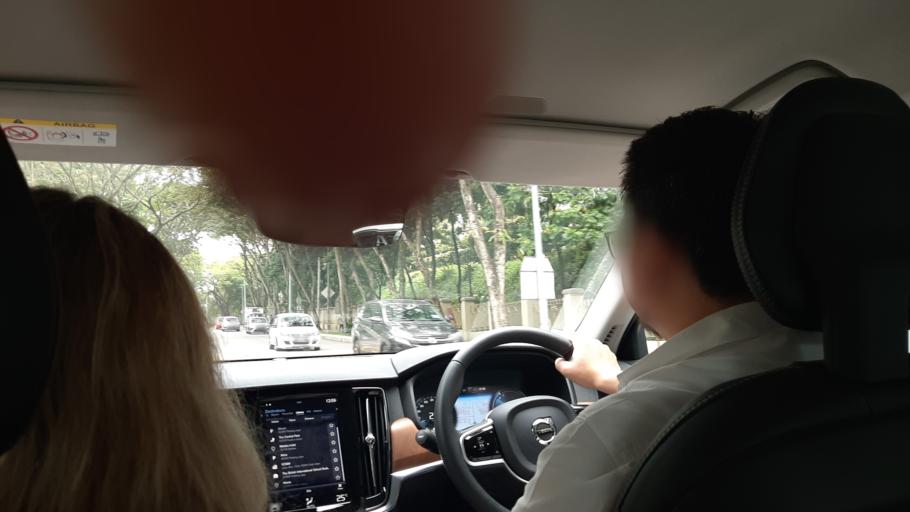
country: MY
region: Kuala Lumpur
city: Kuala Lumpur
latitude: 3.1684
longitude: 101.6528
